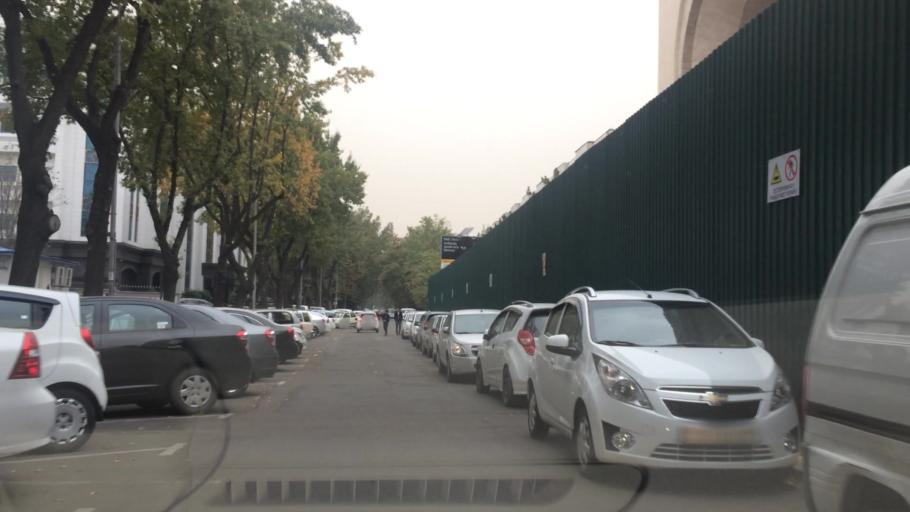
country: UZ
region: Toshkent Shahri
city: Tashkent
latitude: 41.3086
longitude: 69.2774
